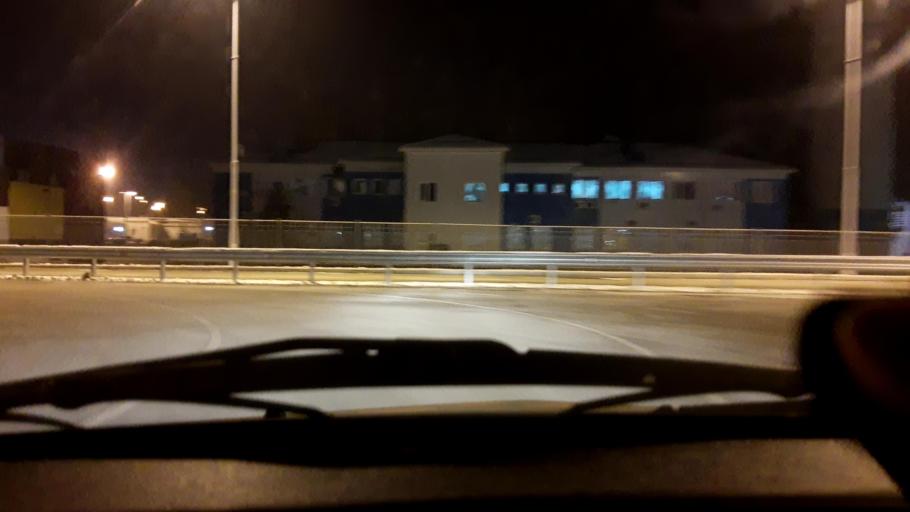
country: RU
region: Bashkortostan
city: Ufa
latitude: 54.5649
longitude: 55.8865
